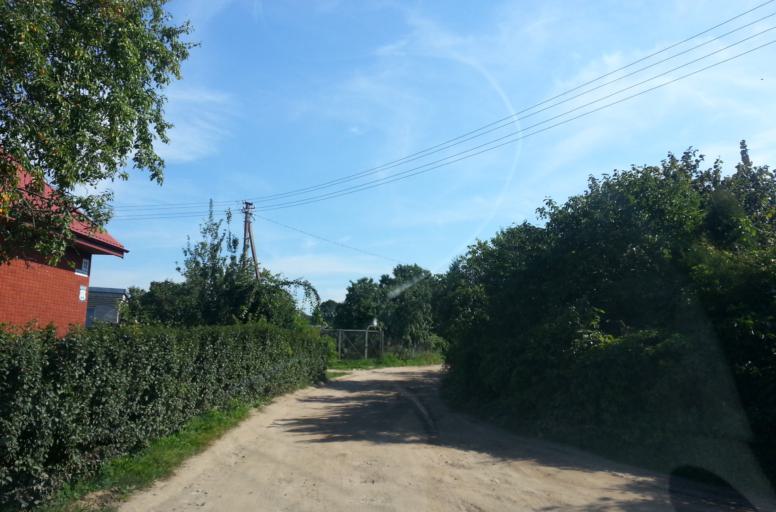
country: LT
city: Grigiskes
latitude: 54.7503
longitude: 25.0246
